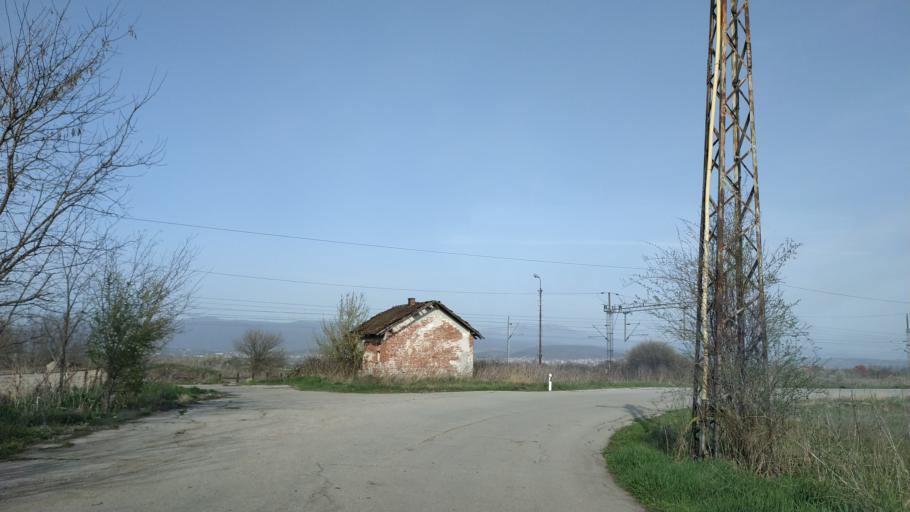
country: RS
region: Central Serbia
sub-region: Nisavski Okrug
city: Aleksinac
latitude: 43.5209
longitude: 21.6536
